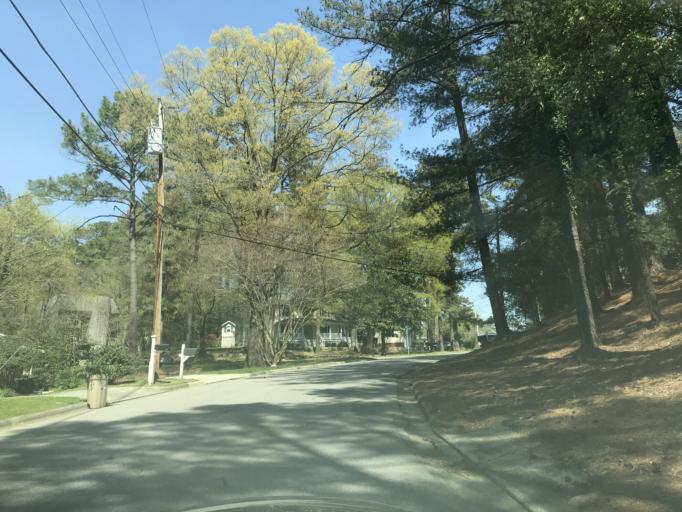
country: US
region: North Carolina
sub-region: Wake County
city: West Raleigh
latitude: 35.8277
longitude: -78.6367
